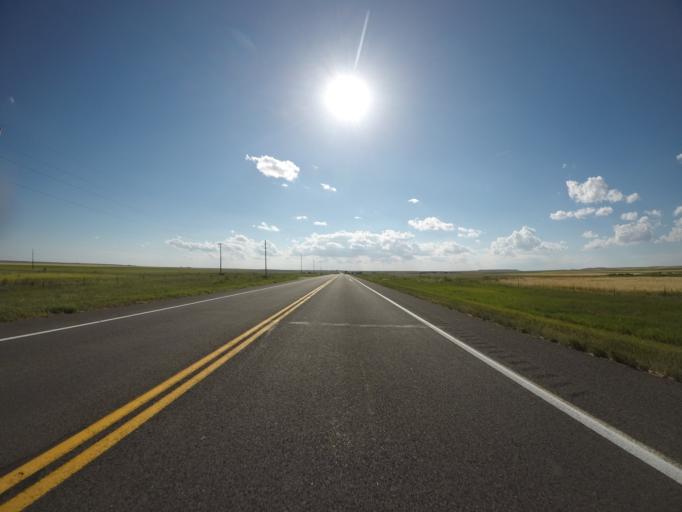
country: US
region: Colorado
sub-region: Morgan County
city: Fort Morgan
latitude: 40.6111
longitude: -103.7810
